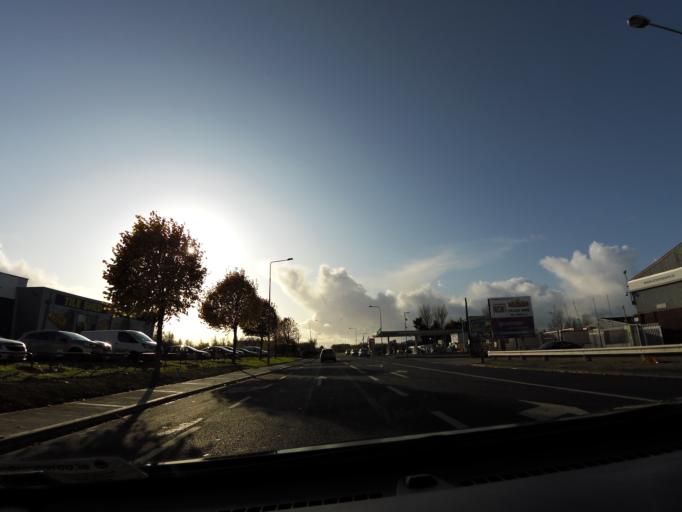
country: IE
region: Munster
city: Moyross
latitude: 52.6496
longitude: -8.6631
